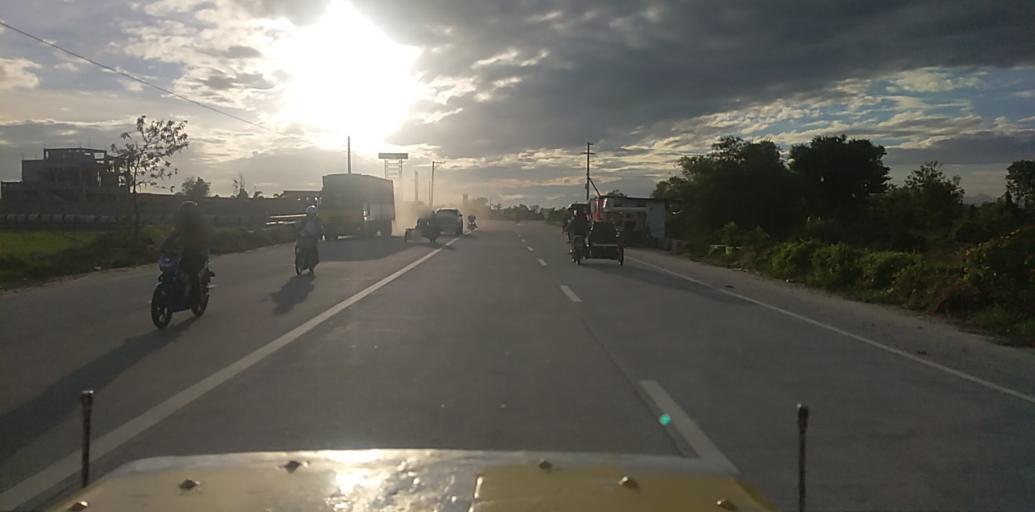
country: PH
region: Central Luzon
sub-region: Province of Pampanga
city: Malino
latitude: 15.1343
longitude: 120.6827
